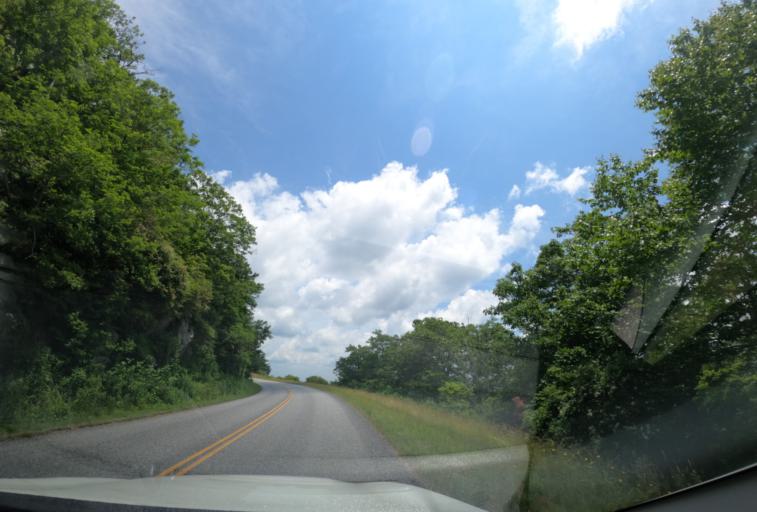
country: US
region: North Carolina
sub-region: Haywood County
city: Canton
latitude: 35.3949
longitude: -82.7660
